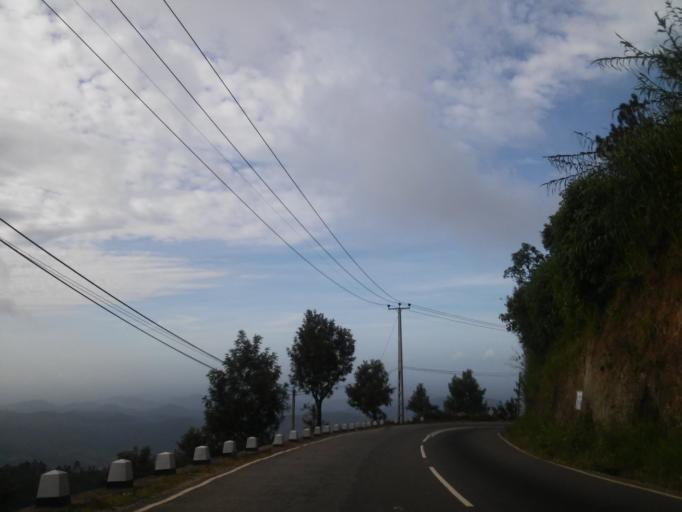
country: LK
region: Uva
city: Haputale
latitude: 6.7642
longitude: 80.9535
